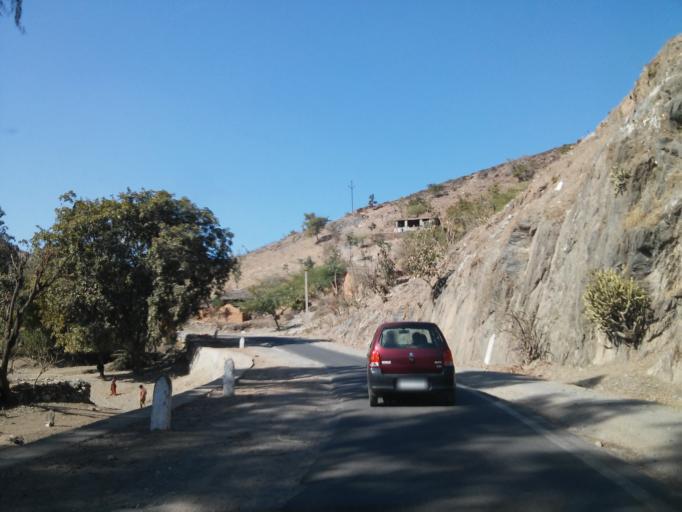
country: IN
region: Rajasthan
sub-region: Udaipur
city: Udaipur
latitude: 24.4986
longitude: 73.6039
